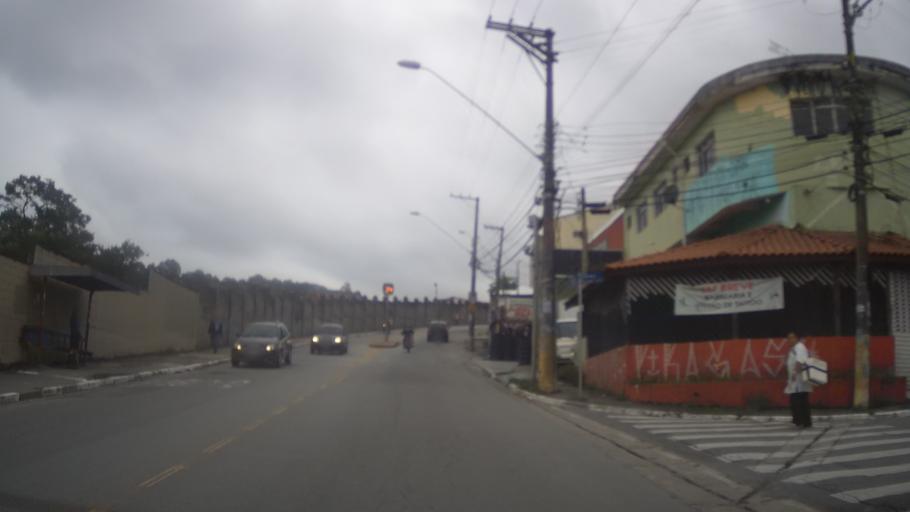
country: BR
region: Sao Paulo
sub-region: Guarulhos
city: Guarulhos
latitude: -23.4286
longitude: -46.5363
